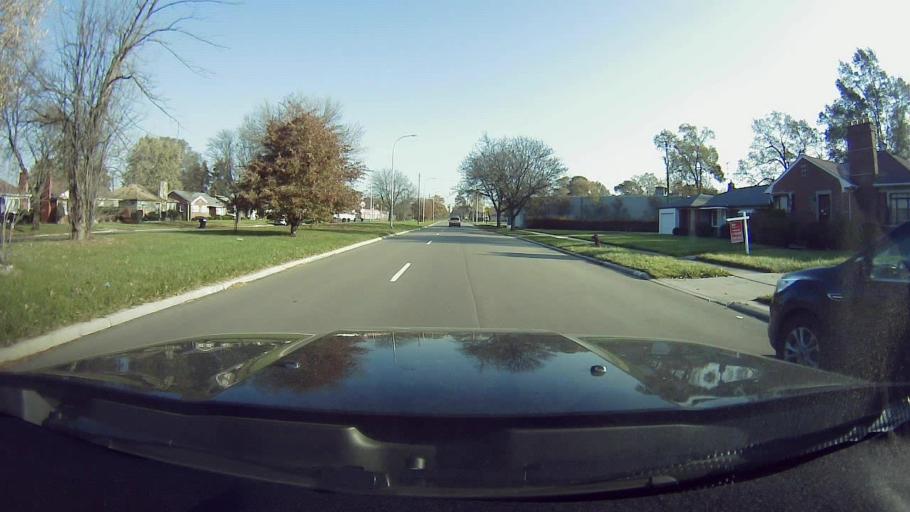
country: US
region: Michigan
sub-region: Wayne County
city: Dearborn
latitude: 42.3607
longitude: -83.1591
